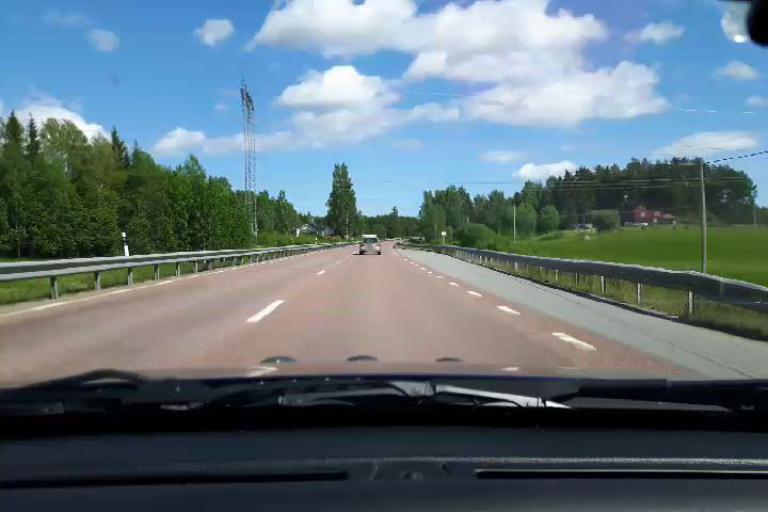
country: SE
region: Gaevleborg
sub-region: Hudiksvalls Kommun
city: Sorforsa
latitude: 61.7399
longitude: 16.8974
